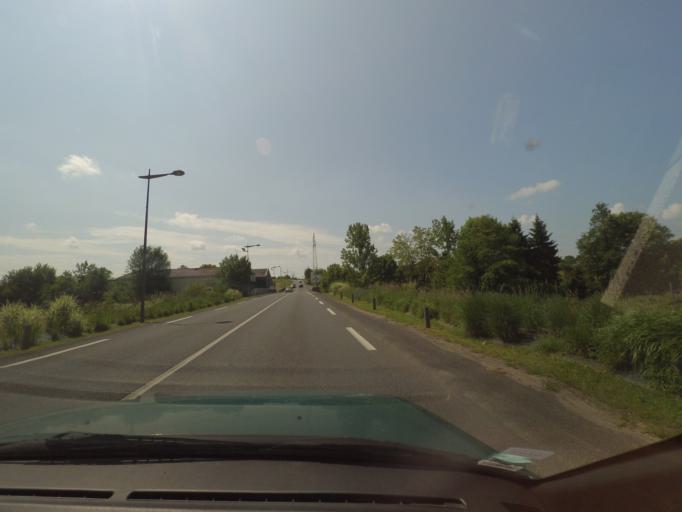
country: FR
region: Pays de la Loire
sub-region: Departement de la Loire-Atlantique
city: Mouzillon
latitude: 47.1393
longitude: -1.2823
